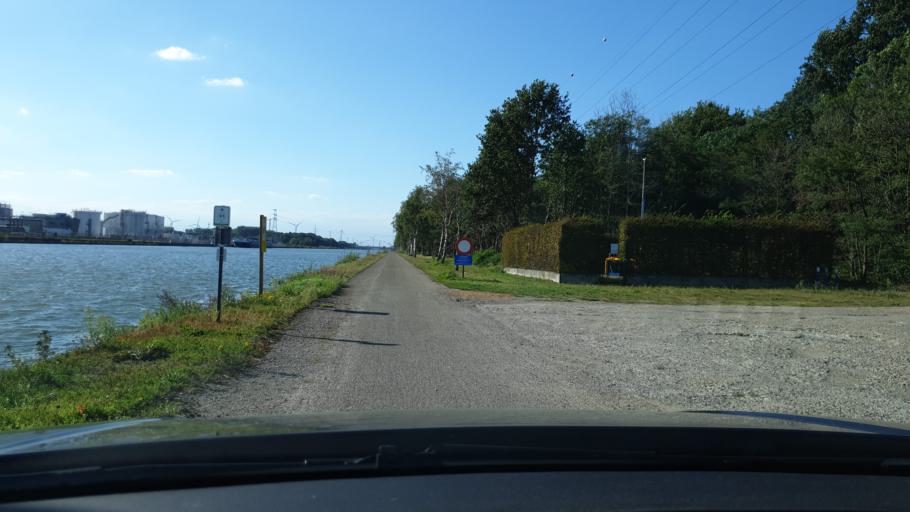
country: BE
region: Flanders
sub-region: Provincie Antwerpen
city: Laakdal
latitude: 51.1177
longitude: 5.0139
